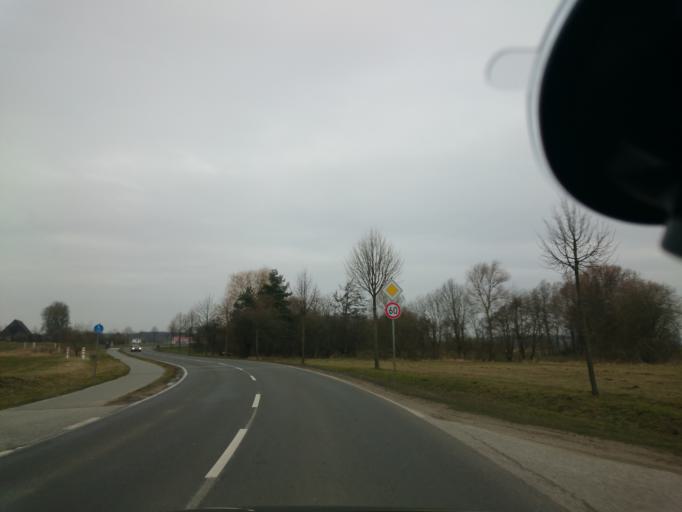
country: DE
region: Mecklenburg-Vorpommern
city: Bad Doberan
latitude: 54.1124
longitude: 11.9205
